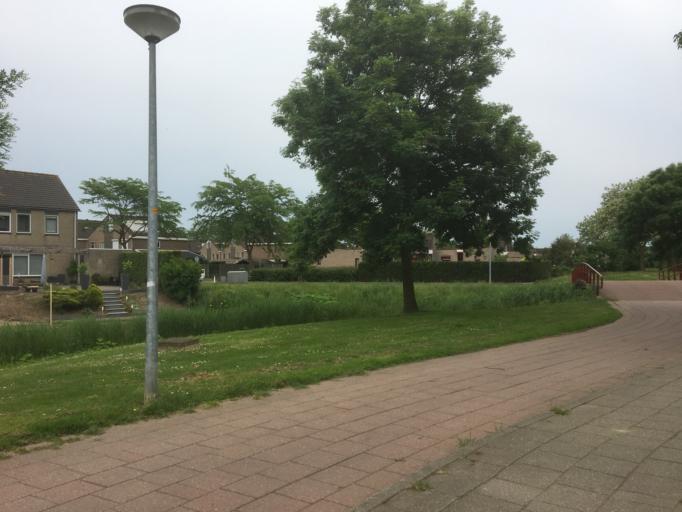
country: NL
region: Gelderland
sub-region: Gemeente Duiven
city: Duiven
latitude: 51.9392
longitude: 6.0136
